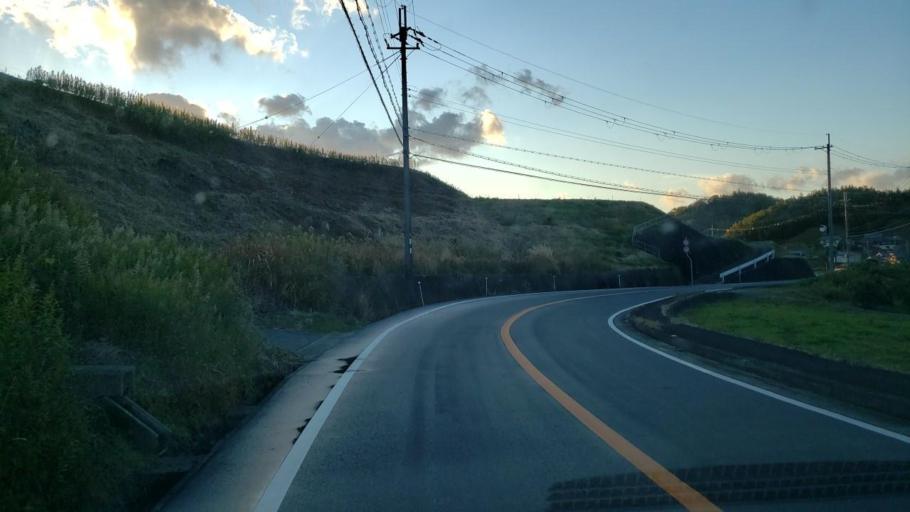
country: JP
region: Hyogo
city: Sumoto
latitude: 34.4006
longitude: 134.8286
